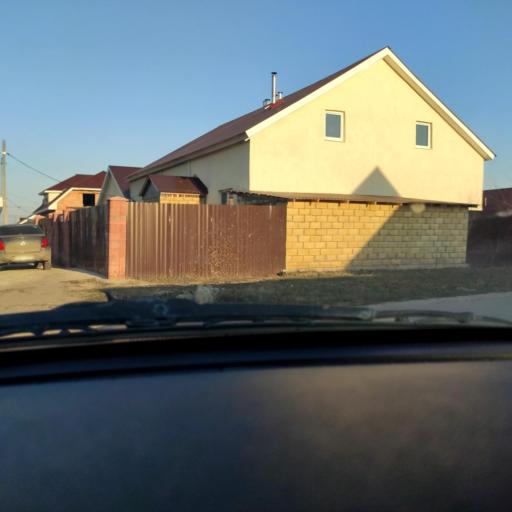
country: RU
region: Samara
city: Podstepki
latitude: 53.5757
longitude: 49.1135
